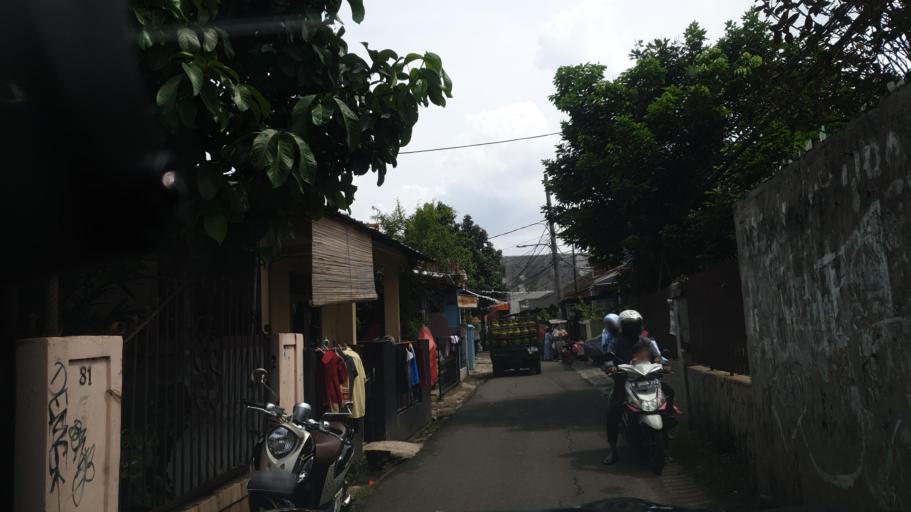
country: ID
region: West Java
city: Pamulang
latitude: -6.3389
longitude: 106.7697
